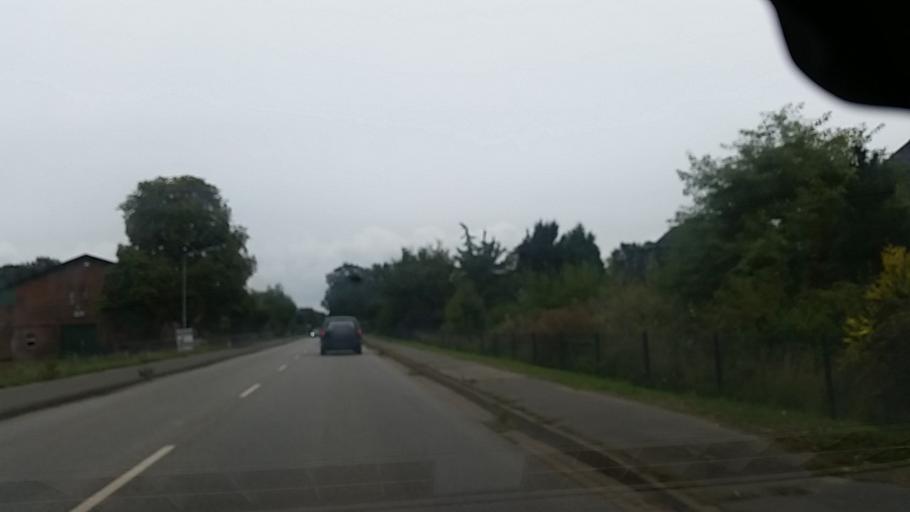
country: DE
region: Schleswig-Holstein
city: Kayhude
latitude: 53.7660
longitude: 10.1264
